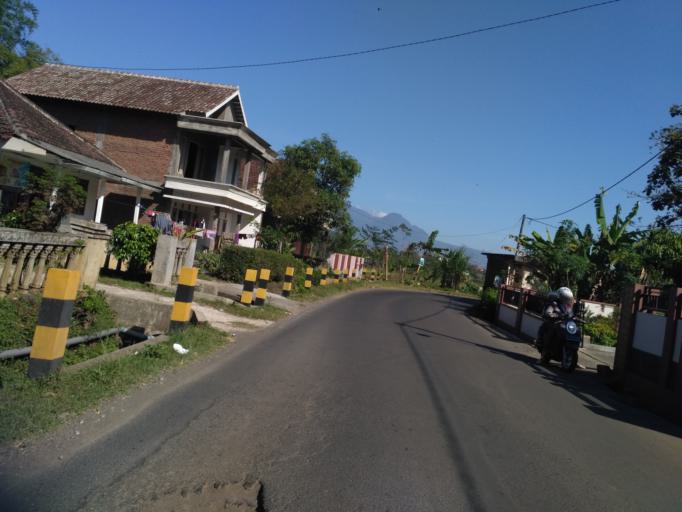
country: ID
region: East Java
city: Singosari
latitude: -7.9267
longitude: 112.6669
